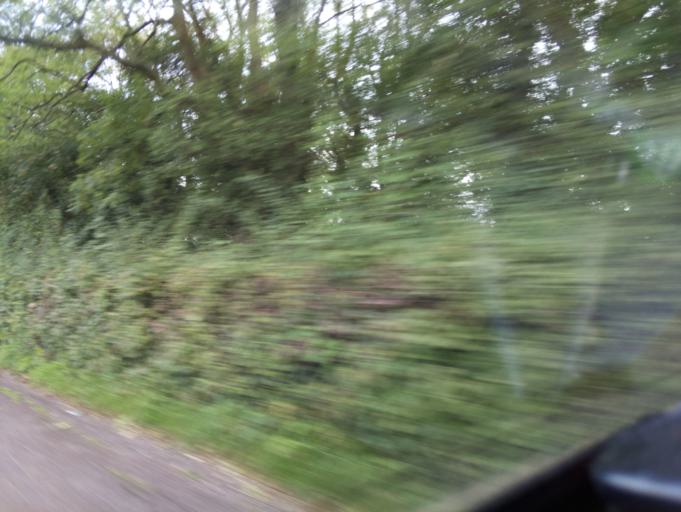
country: GB
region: England
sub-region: South Gloucestershire
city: Alveston
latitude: 51.5853
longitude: -2.5153
